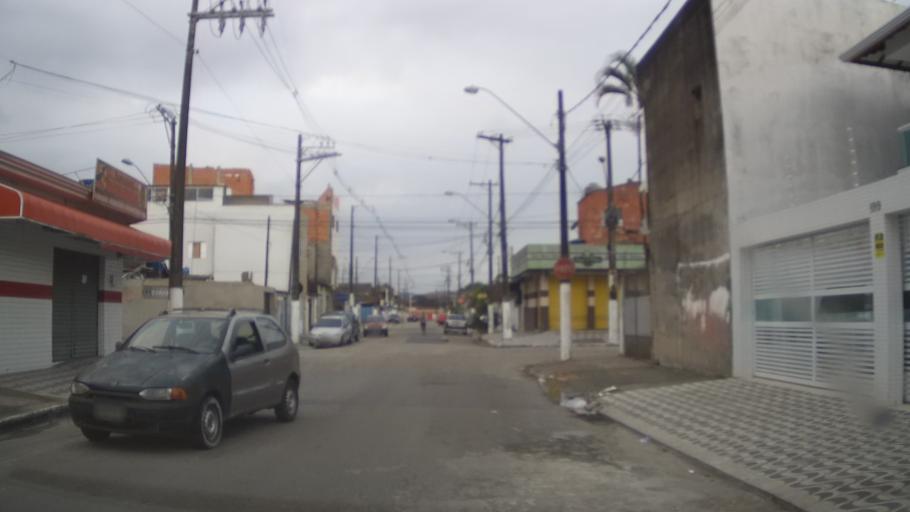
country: BR
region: Sao Paulo
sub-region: Praia Grande
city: Praia Grande
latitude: -24.0082
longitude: -46.4417
